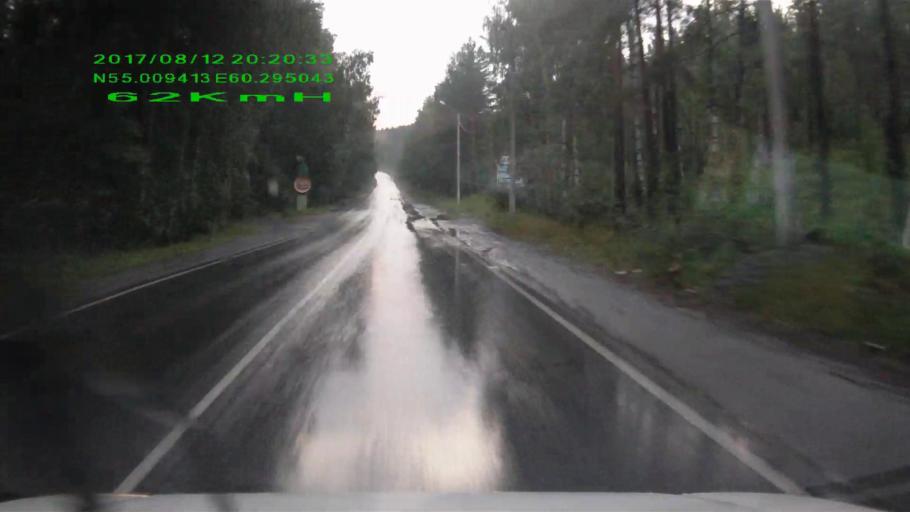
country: RU
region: Chelyabinsk
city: Chebarkul'
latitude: 55.0096
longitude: 60.2945
